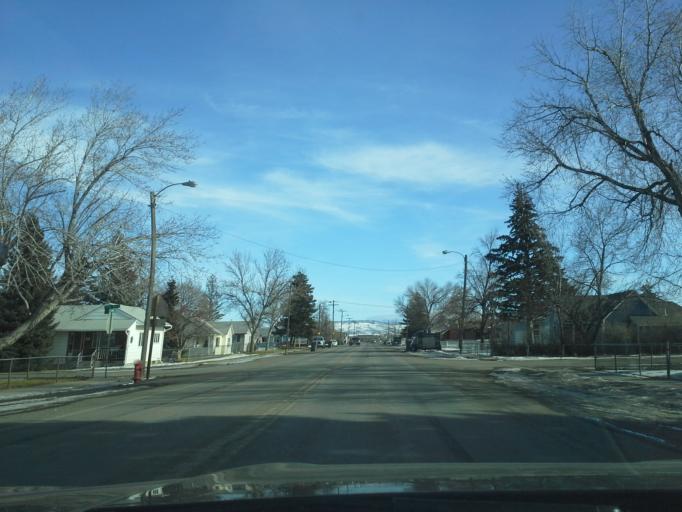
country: US
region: Montana
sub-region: Lewis and Clark County
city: East Helena
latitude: 46.5895
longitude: -111.9133
